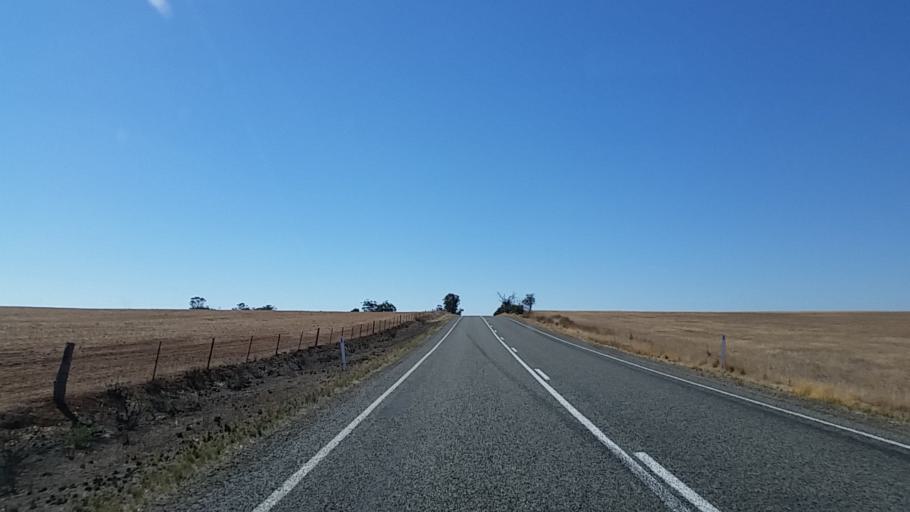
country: AU
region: South Australia
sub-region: Northern Areas
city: Jamestown
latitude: -33.3422
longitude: 138.8923
